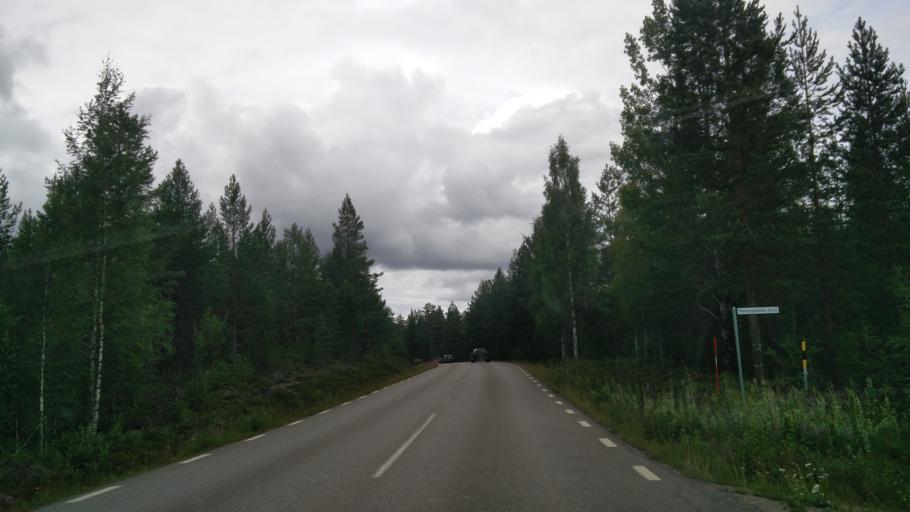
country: NO
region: Hedmark
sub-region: Trysil
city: Innbygda
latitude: 61.1695
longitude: 12.8397
